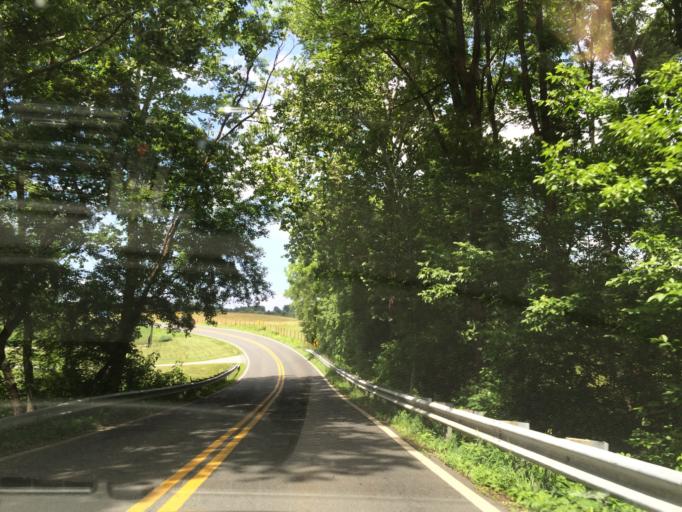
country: US
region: Maryland
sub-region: Carroll County
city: Eldersburg
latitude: 39.4298
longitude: -76.9600
